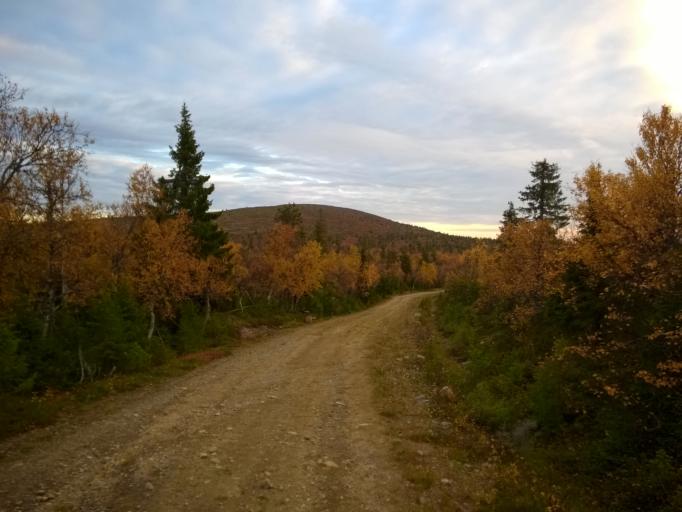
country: FI
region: Lapland
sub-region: Tunturi-Lappi
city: Muonio
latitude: 67.9863
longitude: 24.1130
